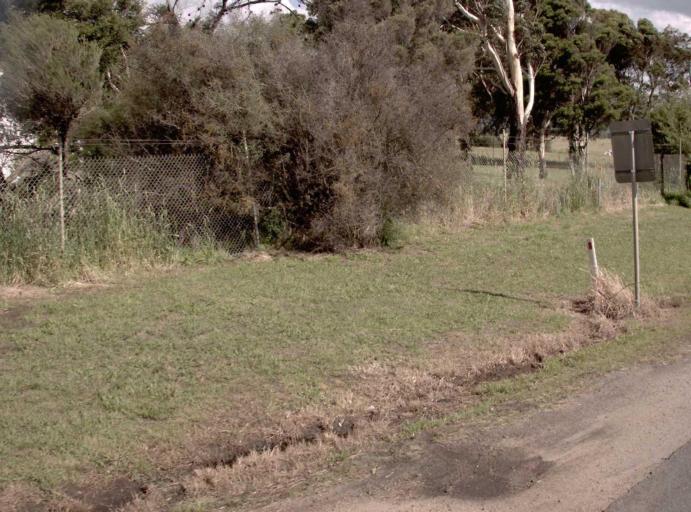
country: AU
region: Victoria
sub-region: Latrobe
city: Morwell
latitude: -38.2500
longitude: 146.4358
